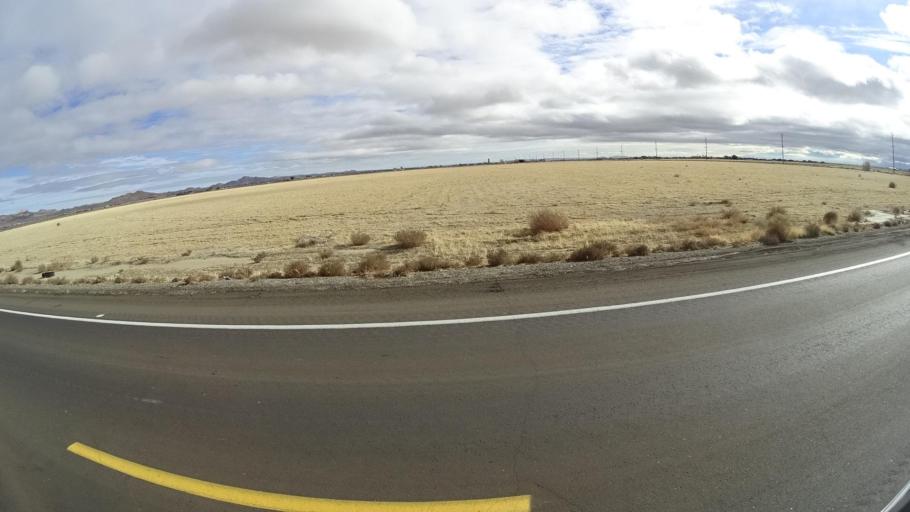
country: US
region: California
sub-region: Kern County
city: Rosamond
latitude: 34.8361
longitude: -118.2912
